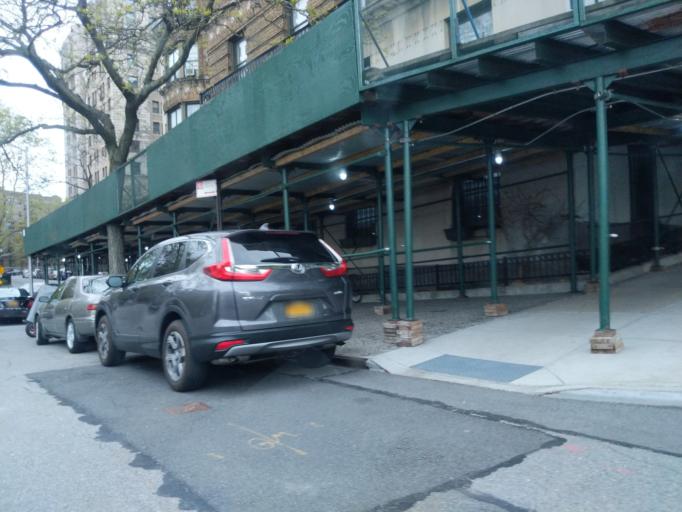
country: US
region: New Jersey
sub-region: Bergen County
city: Fort Lee
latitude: 40.8339
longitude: -73.9482
